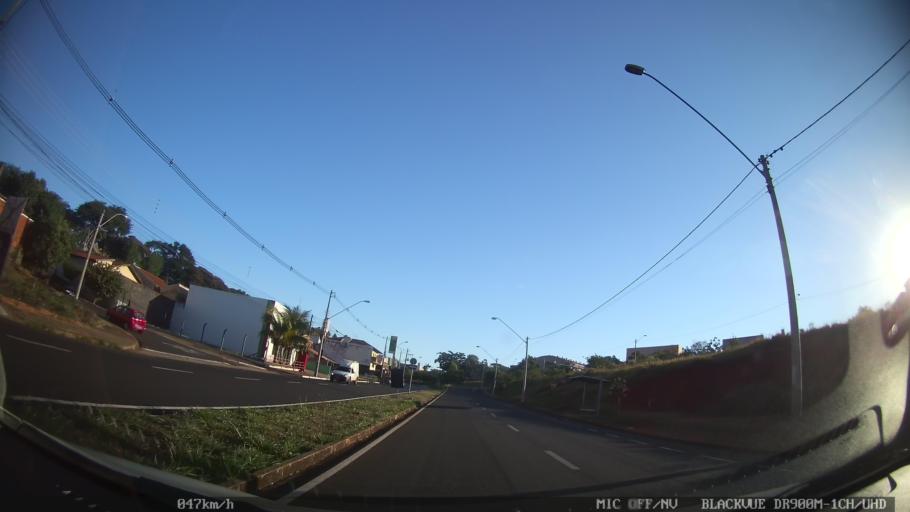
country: BR
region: Sao Paulo
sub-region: Sao Jose Do Rio Preto
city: Sao Jose do Rio Preto
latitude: -20.7927
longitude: -49.3522
